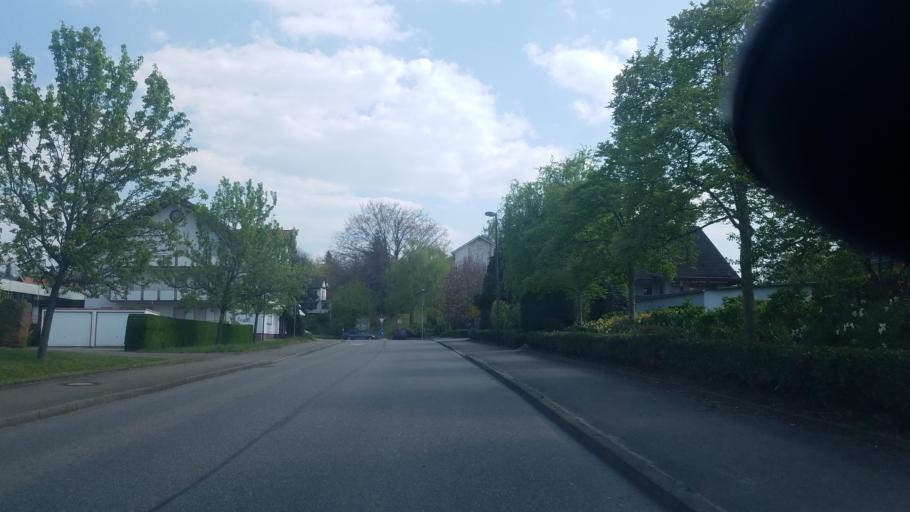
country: DE
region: Baden-Wuerttemberg
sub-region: Freiburg Region
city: Achern
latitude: 48.6244
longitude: 8.0504
